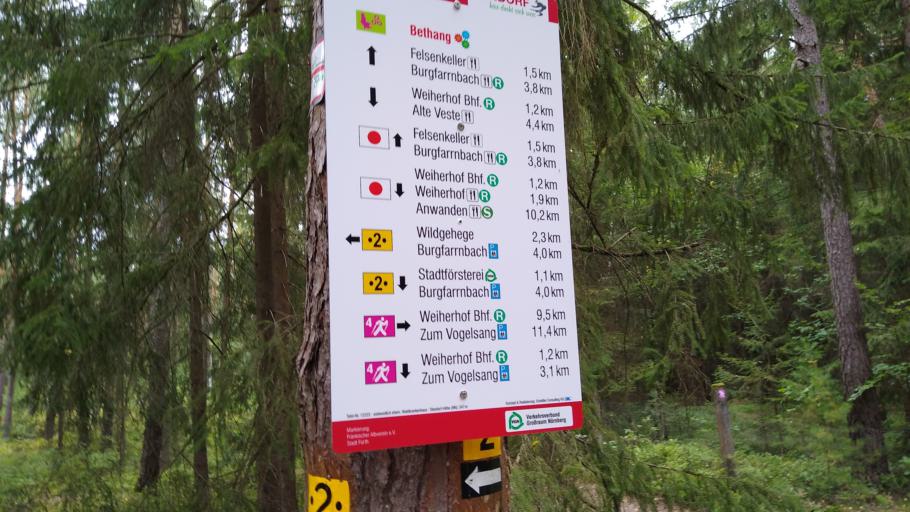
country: DE
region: Bavaria
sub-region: Regierungsbezirk Mittelfranken
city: Zirndorf
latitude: 49.4667
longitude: 10.9219
